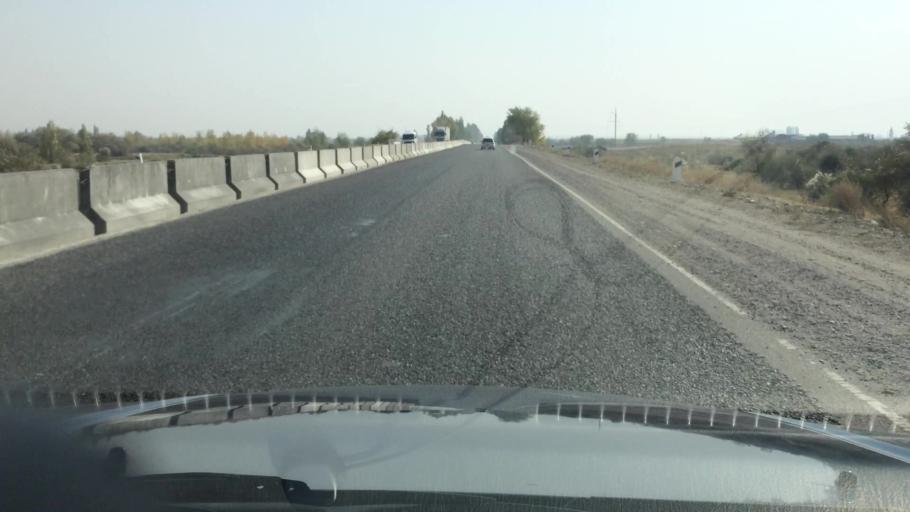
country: KG
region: Chuy
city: Kant
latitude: 42.9710
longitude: 74.9017
